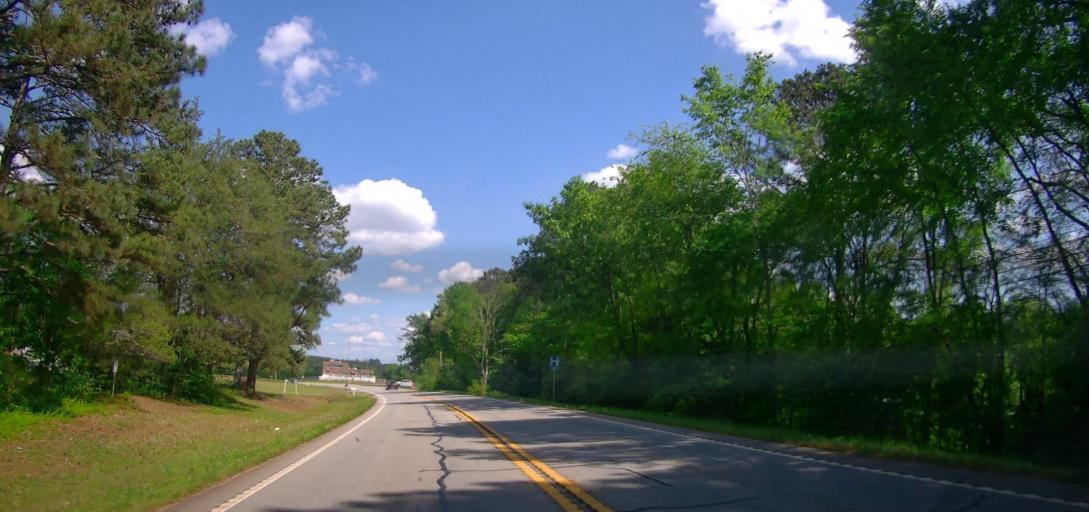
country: US
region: Georgia
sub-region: Greene County
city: Greensboro
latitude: 33.5717
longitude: -83.2409
